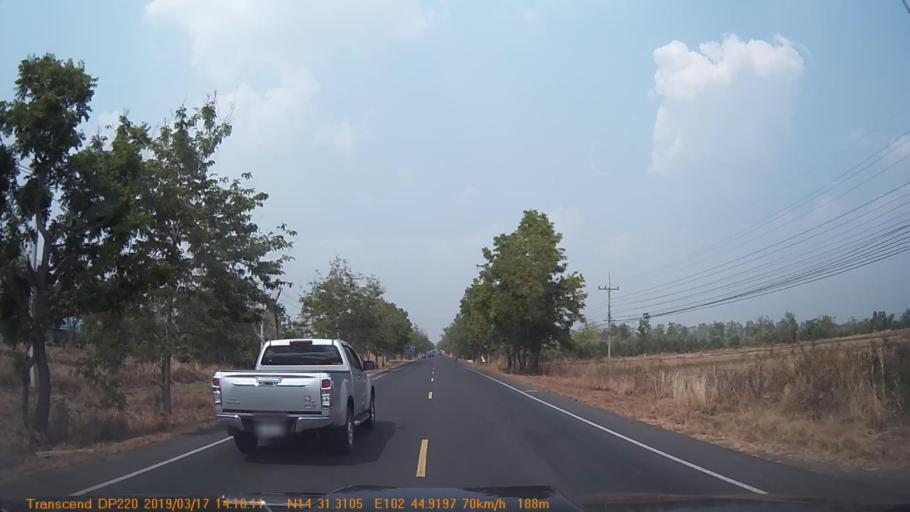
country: TH
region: Buriram
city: Pa Kham
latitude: 14.5221
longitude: 102.7488
